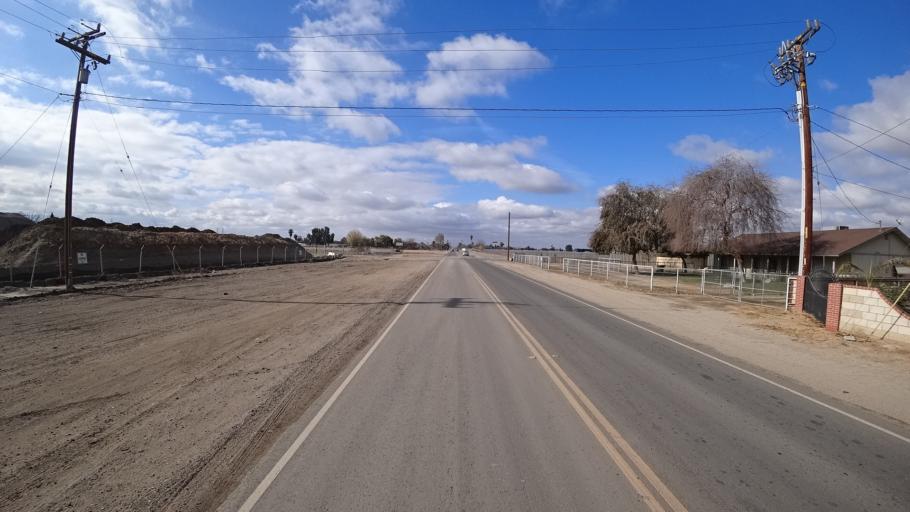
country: US
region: California
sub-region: Kern County
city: Greenfield
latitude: 35.3177
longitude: -118.9929
